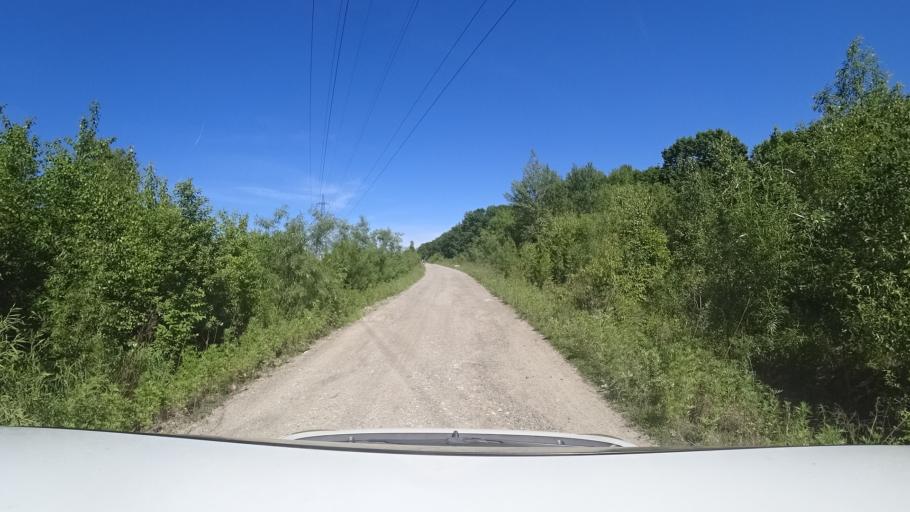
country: RU
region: Khabarovsk Krai
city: Topolevo
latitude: 48.5609
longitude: 135.1896
